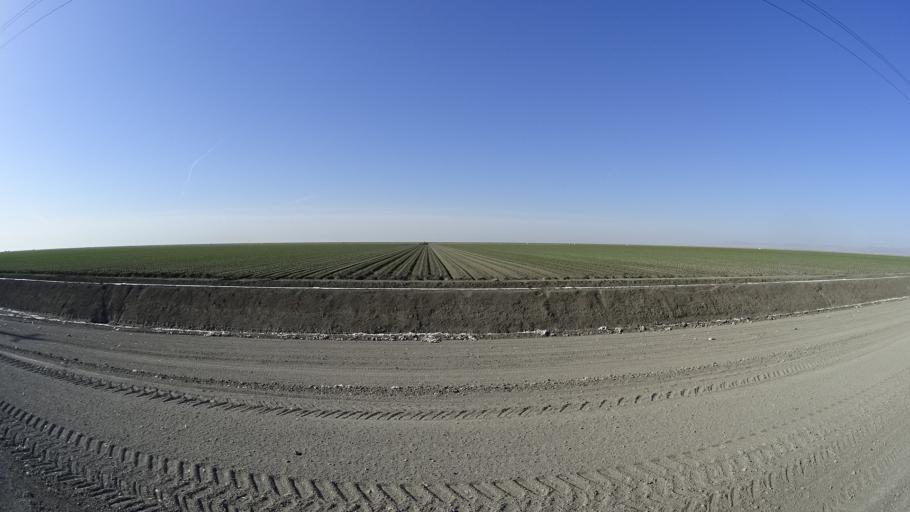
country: US
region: California
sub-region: Kings County
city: Stratford
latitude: 36.0797
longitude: -119.7682
